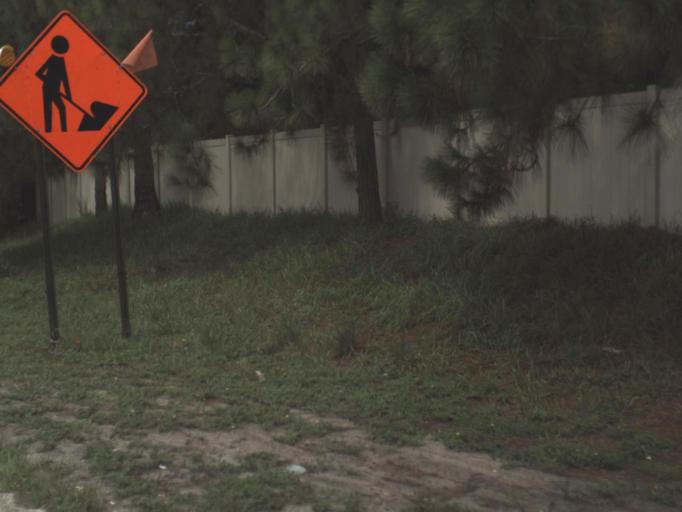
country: US
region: Florida
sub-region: Pasco County
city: Trinity
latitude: 28.1993
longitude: -82.6973
